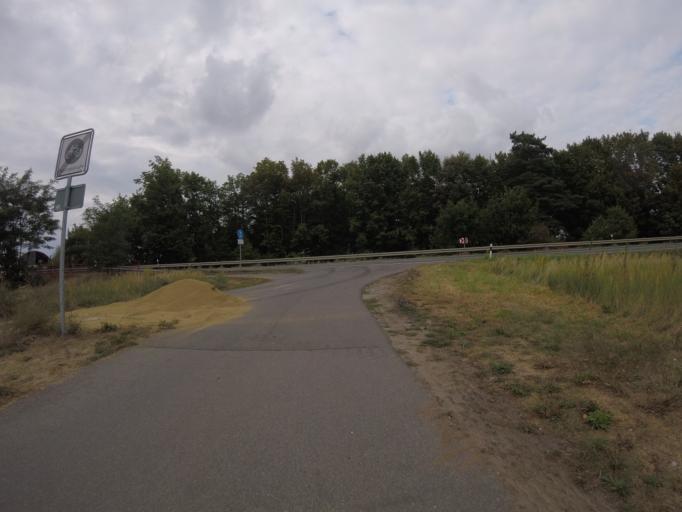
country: DE
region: Brandenburg
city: Liebenwalde
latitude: 52.8722
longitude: 13.3759
